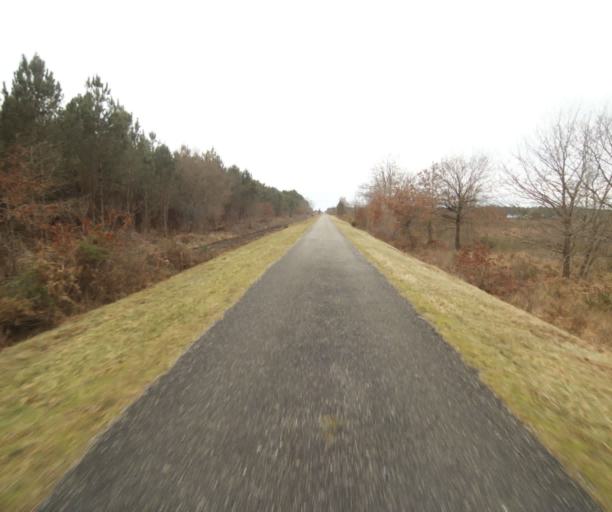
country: FR
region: Aquitaine
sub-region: Departement des Landes
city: Gabarret
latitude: 44.0245
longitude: -0.0508
